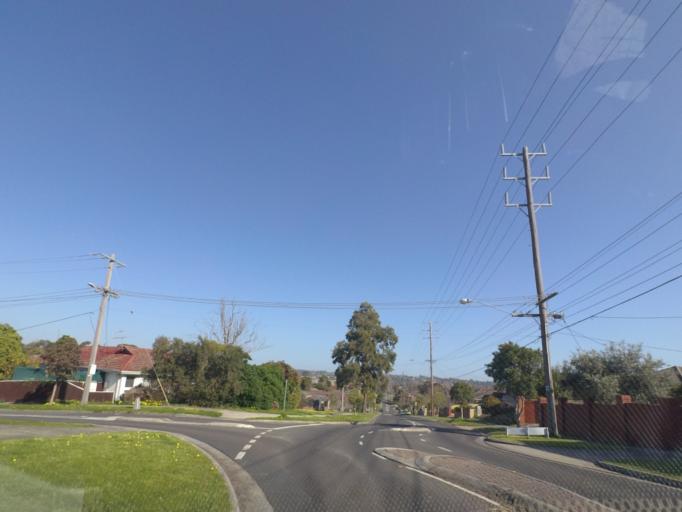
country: AU
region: Victoria
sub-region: Manningham
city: Templestowe Lower
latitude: -37.7748
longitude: 145.1044
